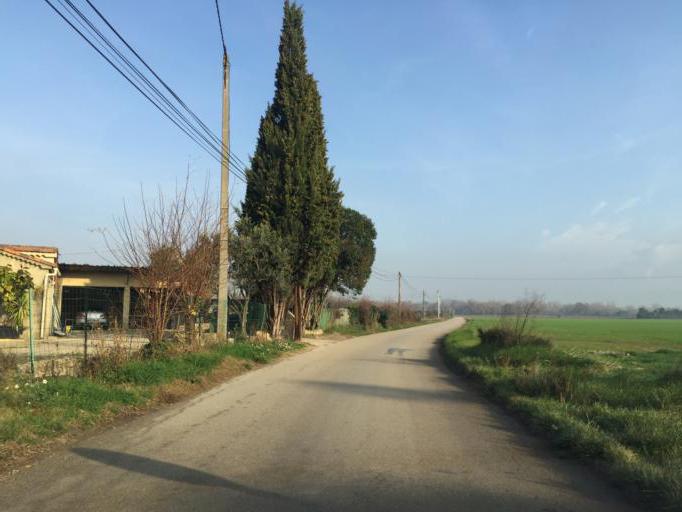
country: FR
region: Provence-Alpes-Cote d'Azur
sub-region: Departement du Vaucluse
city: Jonquieres
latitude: 44.0961
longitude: 4.9100
